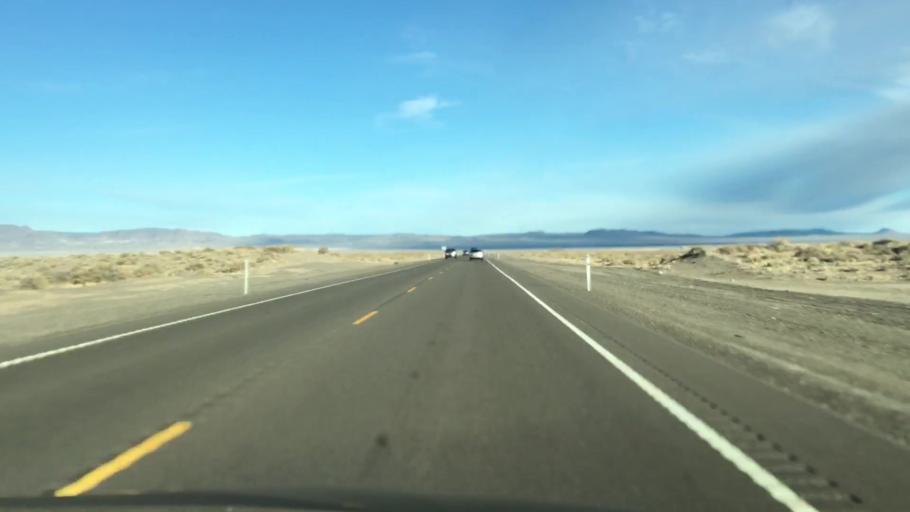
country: US
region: Nevada
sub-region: Nye County
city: Tonopah
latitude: 38.1358
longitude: -117.5124
